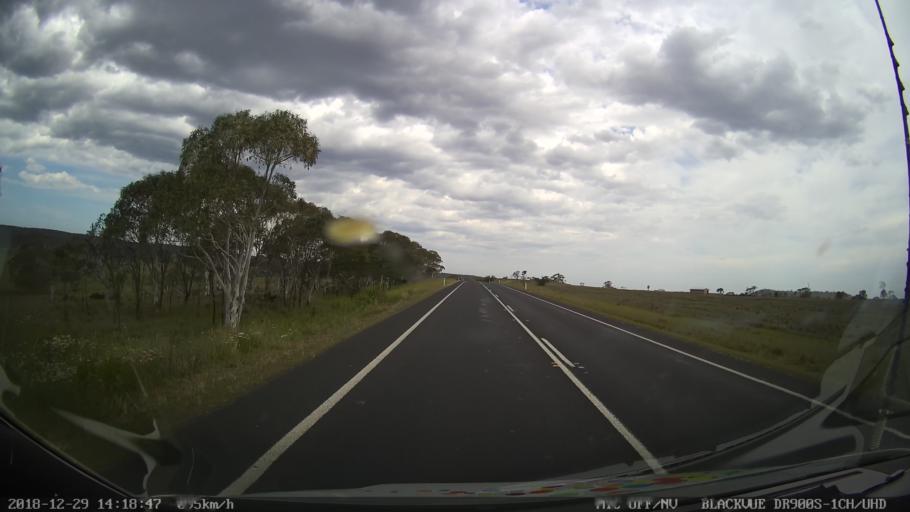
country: AU
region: New South Wales
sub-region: Cooma-Monaro
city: Cooma
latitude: -36.4920
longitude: 149.2731
